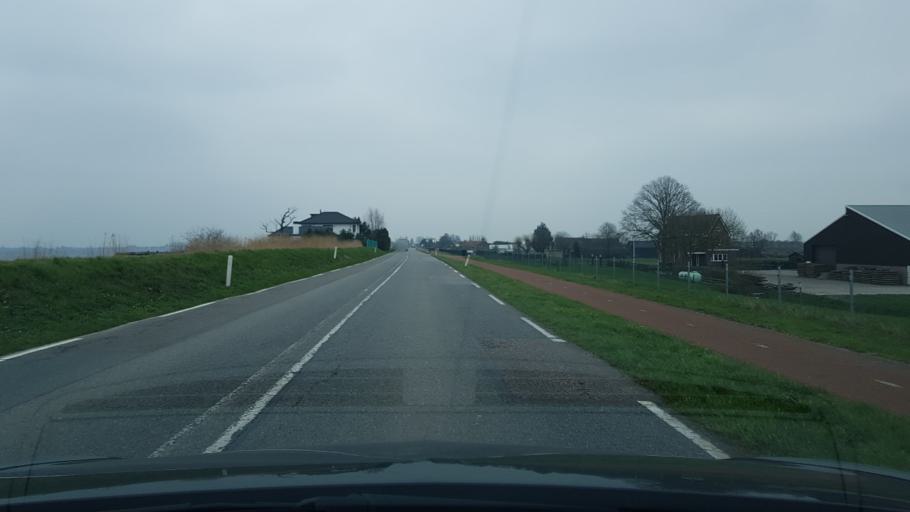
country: NL
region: South Holland
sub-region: Gemeente Kaag en Braassem
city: Leimuiden
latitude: 52.2337
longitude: 4.7058
